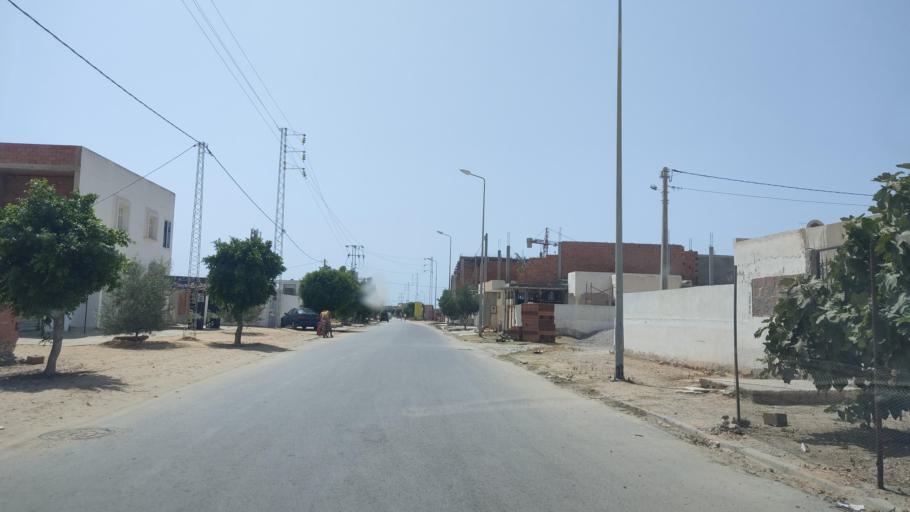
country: TN
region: Safaqis
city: Sfax
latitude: 34.6706
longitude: 10.7050
